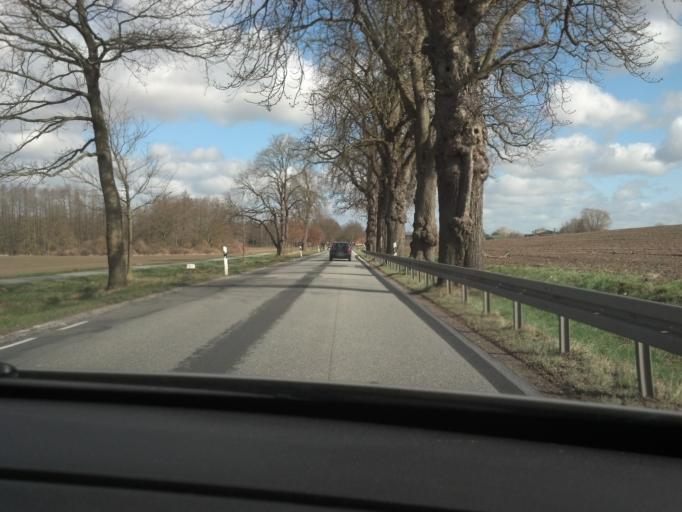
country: DE
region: Mecklenburg-Vorpommern
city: Boizenburg
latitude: 53.4192
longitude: 10.7448
